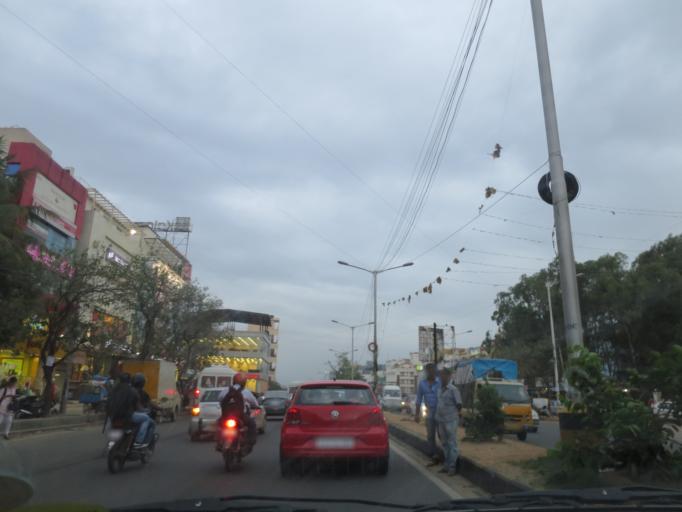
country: IN
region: Karnataka
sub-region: Bangalore Urban
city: Bangalore
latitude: 12.9604
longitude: 77.7014
